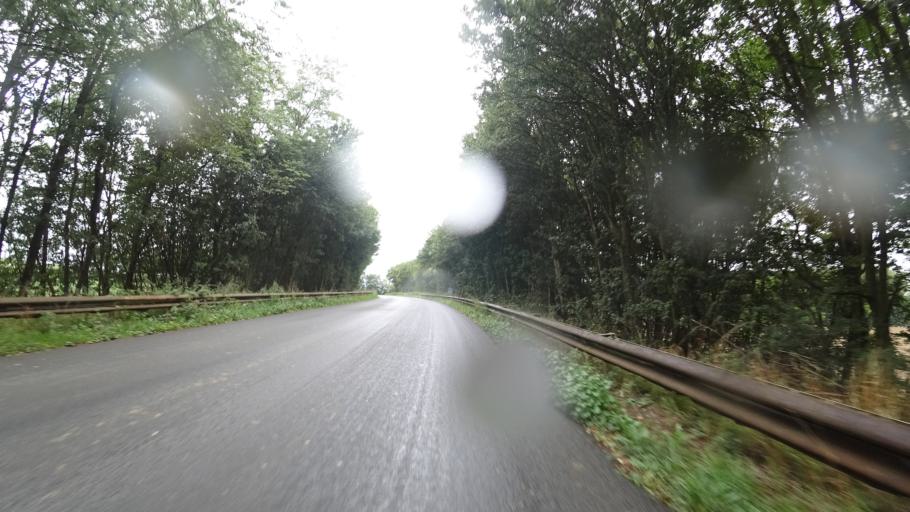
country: BE
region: Wallonia
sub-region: Province de Namur
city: Namur
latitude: 50.5139
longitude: 4.8641
